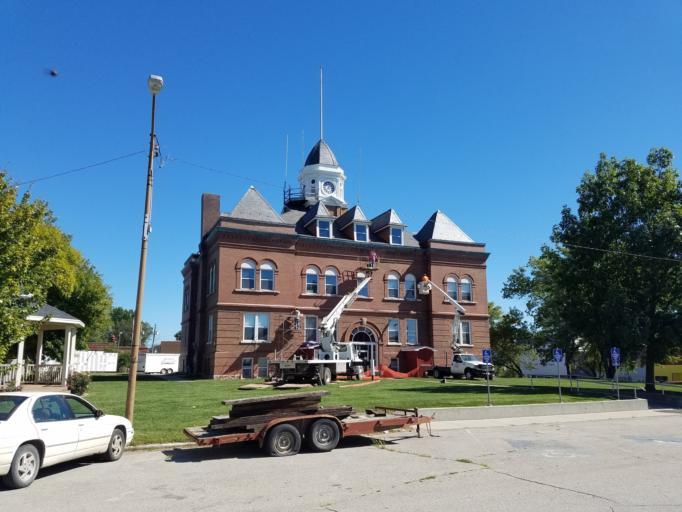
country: US
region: Missouri
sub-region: Worth County
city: Grant City
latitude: 40.4862
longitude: -94.4158
